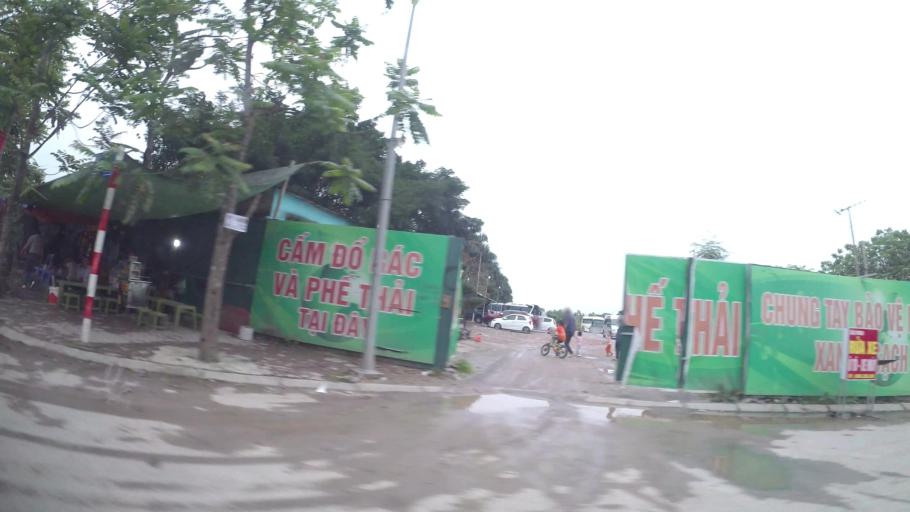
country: VN
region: Ha Noi
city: Hai BaTrung
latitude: 20.9929
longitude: 105.8738
